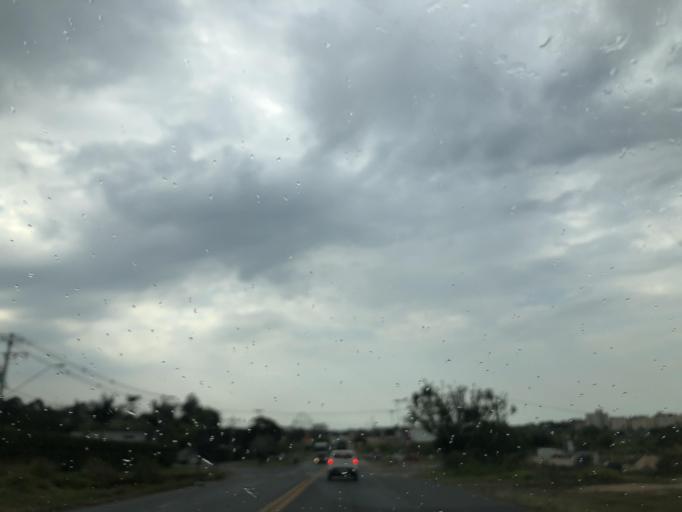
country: BR
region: Sao Paulo
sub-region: Salto De Pirapora
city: Salto de Pirapora
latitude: -23.6495
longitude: -47.5847
